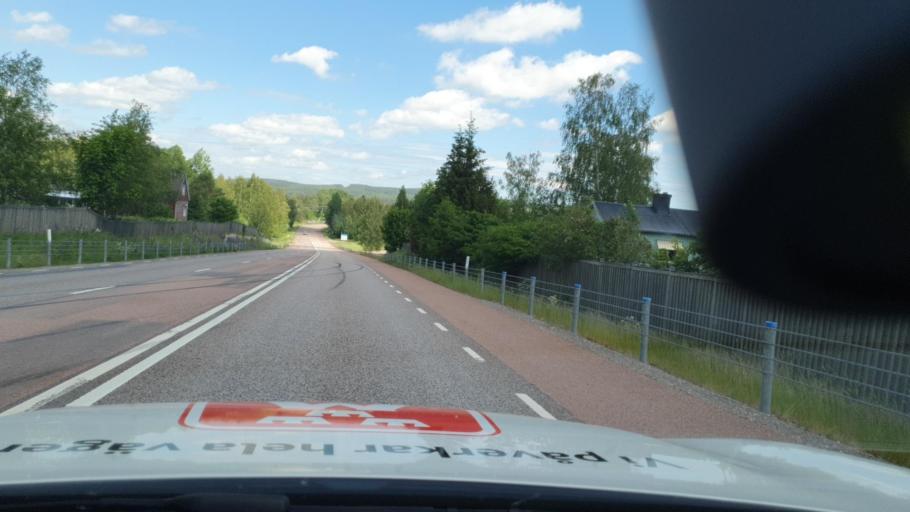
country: SE
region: Vaermland
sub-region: Filipstads Kommun
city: Filipstad
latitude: 59.7087
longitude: 14.1340
